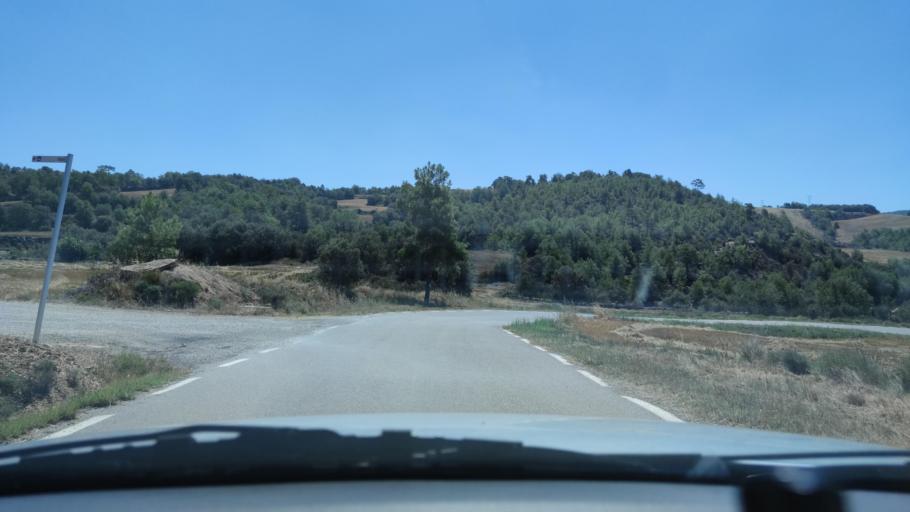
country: ES
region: Catalonia
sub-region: Provincia de Lleida
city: Tora de Riubregos
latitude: 41.8329
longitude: 1.4226
